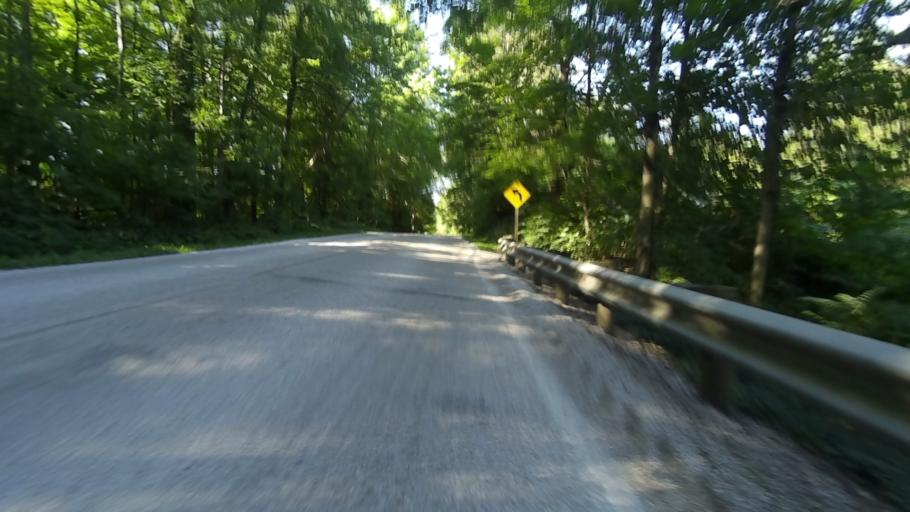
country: US
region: Ohio
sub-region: Portage County
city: Streetsboro
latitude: 41.2517
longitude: -81.2863
